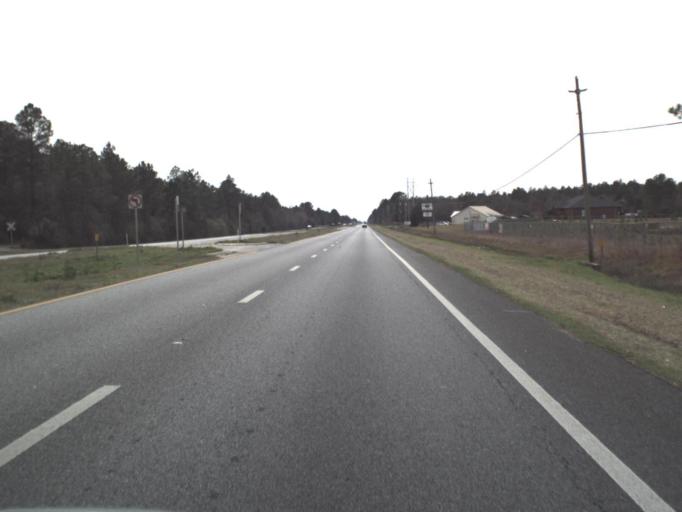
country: US
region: Florida
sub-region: Bay County
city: Youngstown
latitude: 30.3024
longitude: -85.4817
